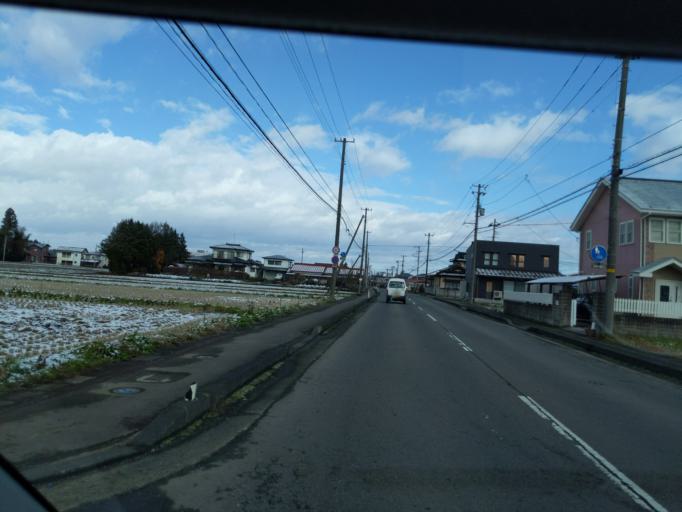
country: JP
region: Iwate
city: Mizusawa
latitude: 39.1129
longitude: 141.1372
